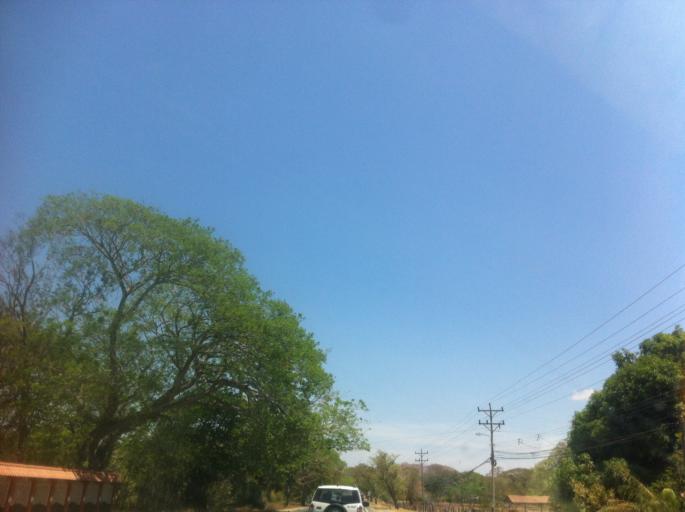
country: CR
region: Guanacaste
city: Belen
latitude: 10.3908
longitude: -85.5867
